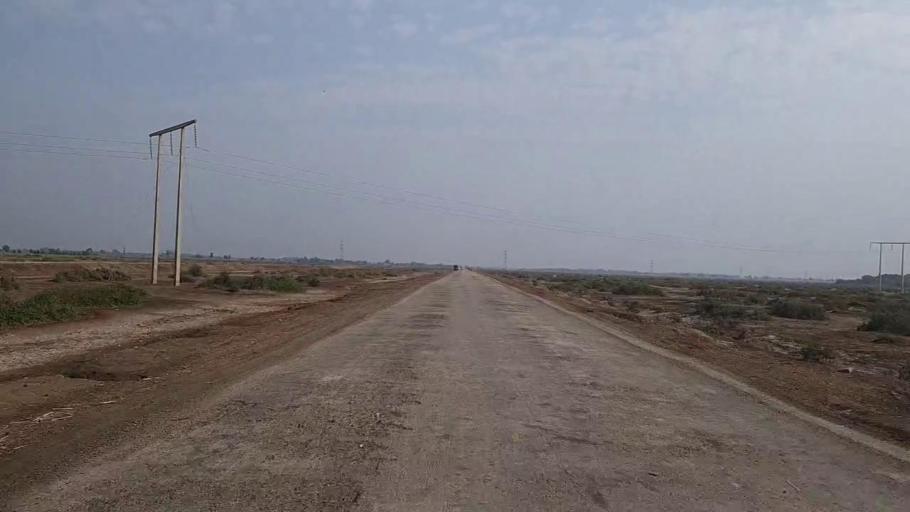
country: PK
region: Sindh
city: Mirpur Khas
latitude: 25.4240
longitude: 69.0216
